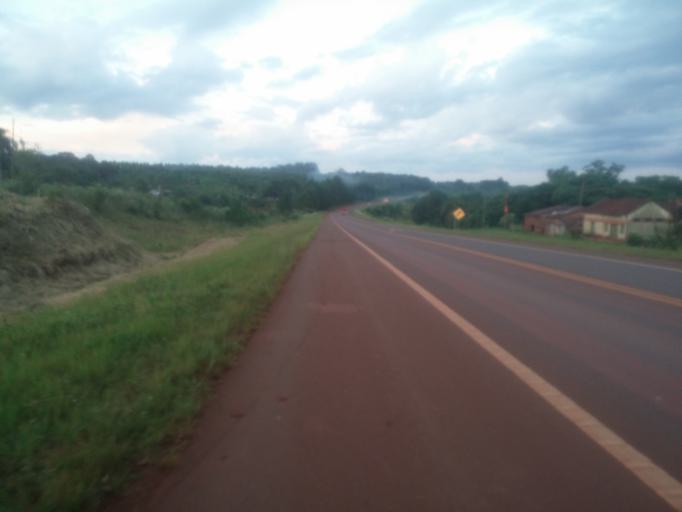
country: AR
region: Misiones
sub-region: Departamento de Obera
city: Obera
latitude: -27.4403
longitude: -55.0826
